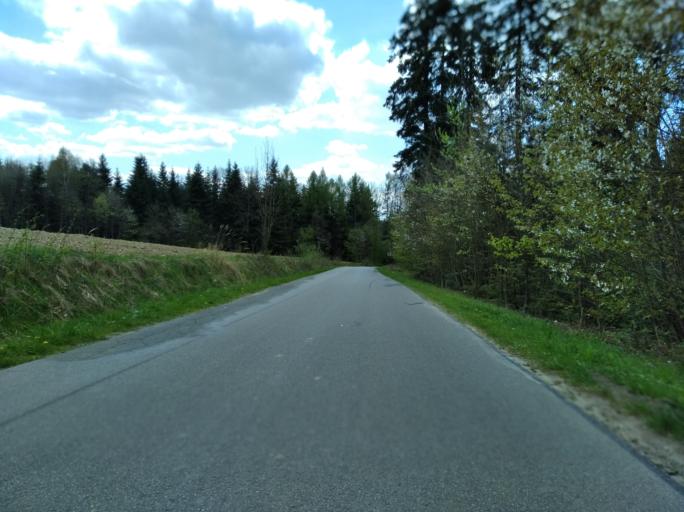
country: PL
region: Subcarpathian Voivodeship
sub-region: Powiat brzozowski
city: Wesola
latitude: 49.7615
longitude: 22.1279
